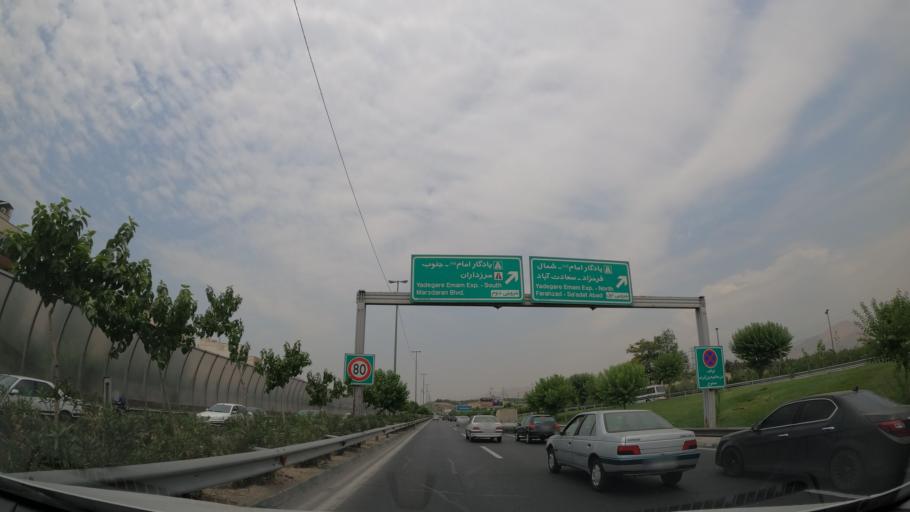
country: IR
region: Tehran
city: Tehran
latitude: 35.7396
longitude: 51.3562
